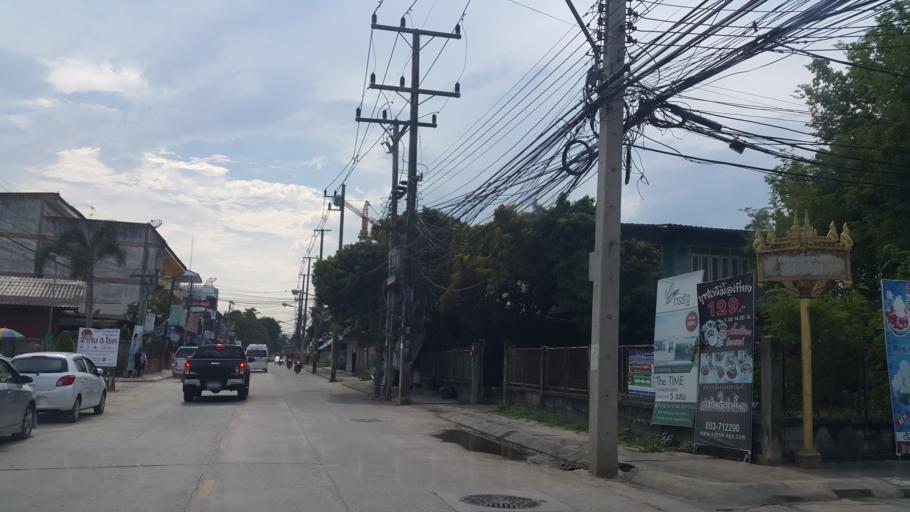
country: TH
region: Chiang Rai
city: Chiang Rai
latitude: 19.9013
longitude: 99.8314
